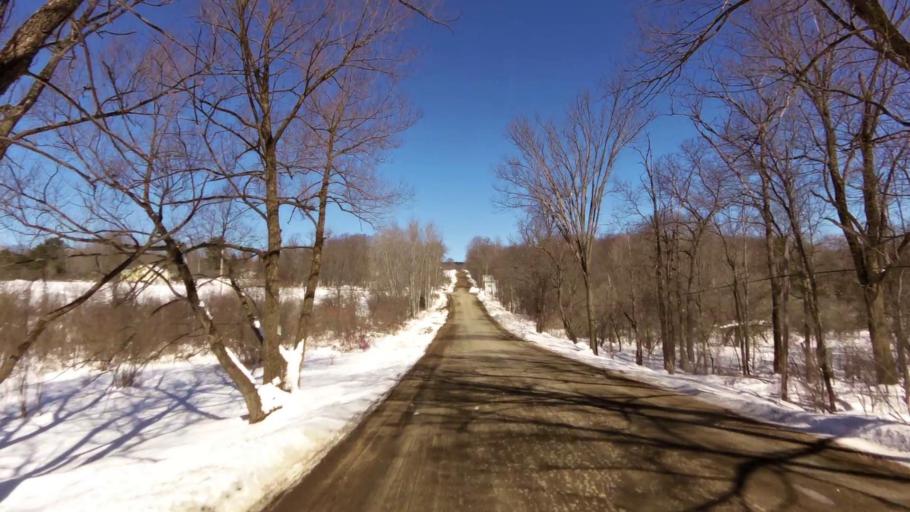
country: US
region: New York
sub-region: Allegany County
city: Cuba
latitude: 42.3378
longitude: -78.2502
